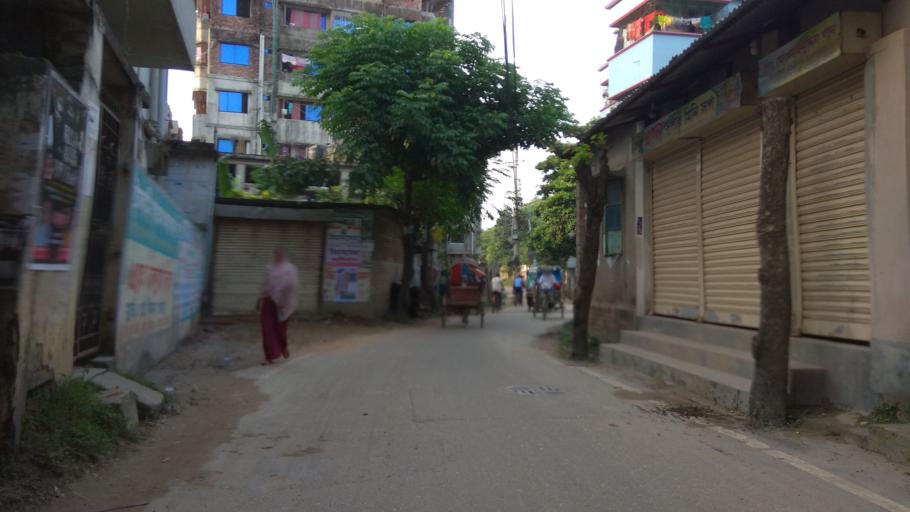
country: BD
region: Dhaka
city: Tungi
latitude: 23.8382
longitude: 90.3874
